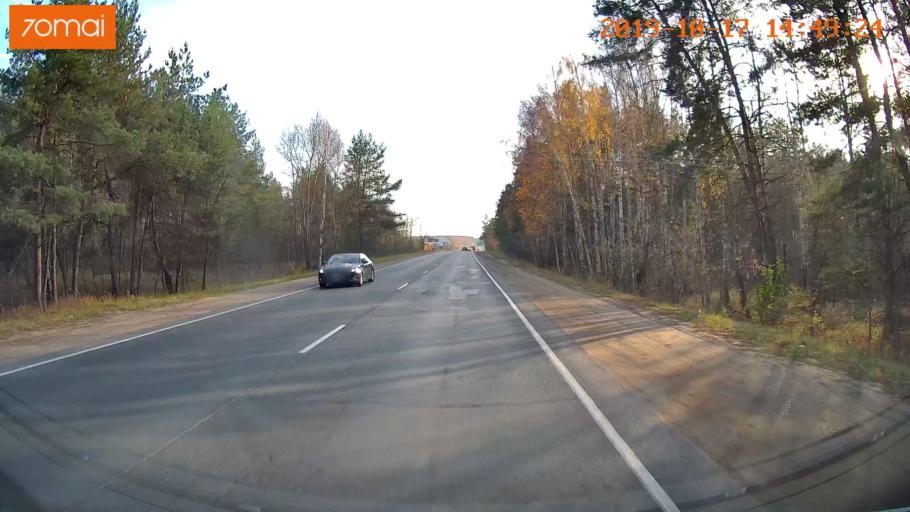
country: RU
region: Rjazan
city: Polyany
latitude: 54.7475
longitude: 39.8399
